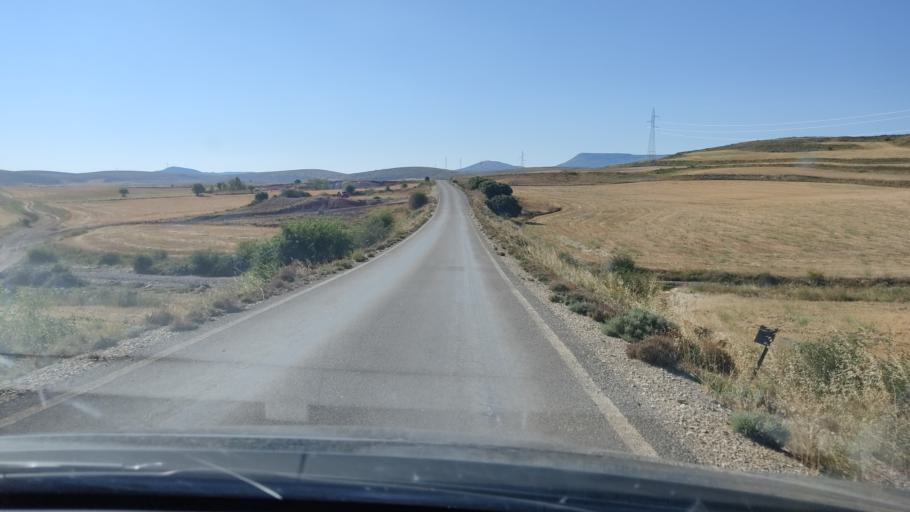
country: ES
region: Aragon
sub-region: Provincia de Teruel
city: Monforte de Moyuela
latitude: 41.0395
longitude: -0.9823
